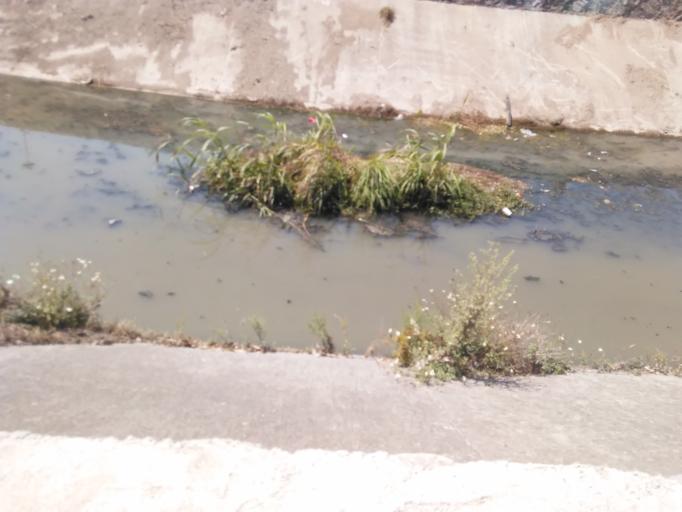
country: MX
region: Nayarit
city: Tepic
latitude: 21.4889
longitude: -104.8751
